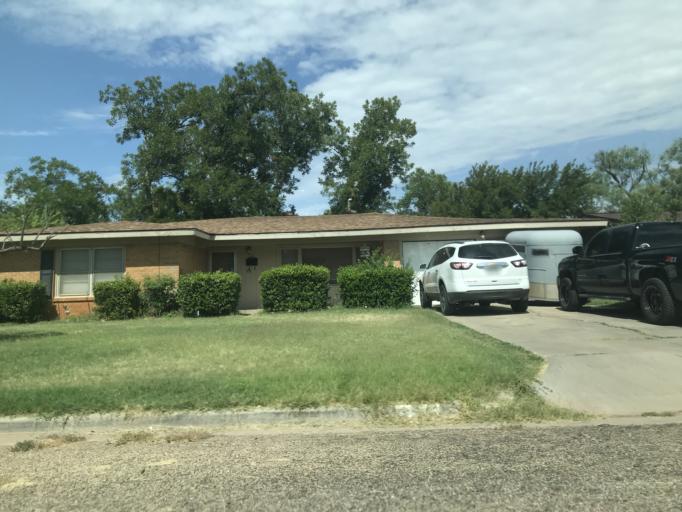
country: US
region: Texas
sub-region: Taylor County
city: Abilene
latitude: 32.4475
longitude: -99.7733
